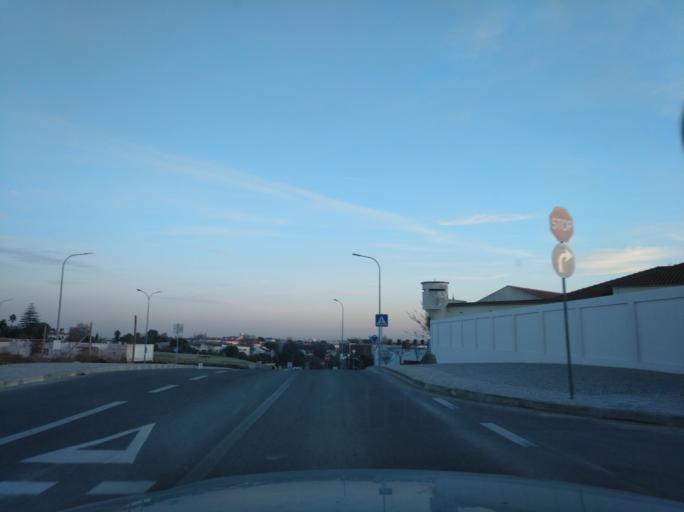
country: PT
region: Lisbon
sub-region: Odivelas
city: Olival do Basto
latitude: 38.7876
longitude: -9.1502
